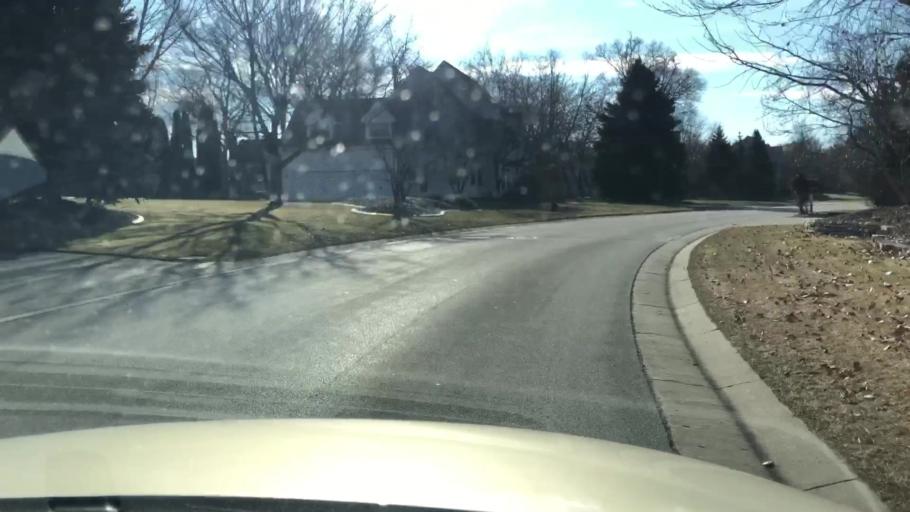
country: US
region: Wisconsin
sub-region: Waukesha County
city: Brookfield
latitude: 43.0710
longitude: -88.1678
